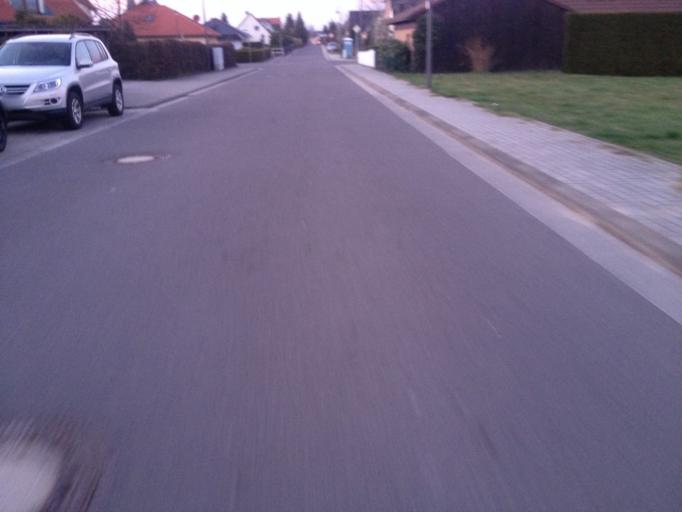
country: DE
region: Brandenburg
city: Drehnow
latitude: 51.8218
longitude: 14.3455
